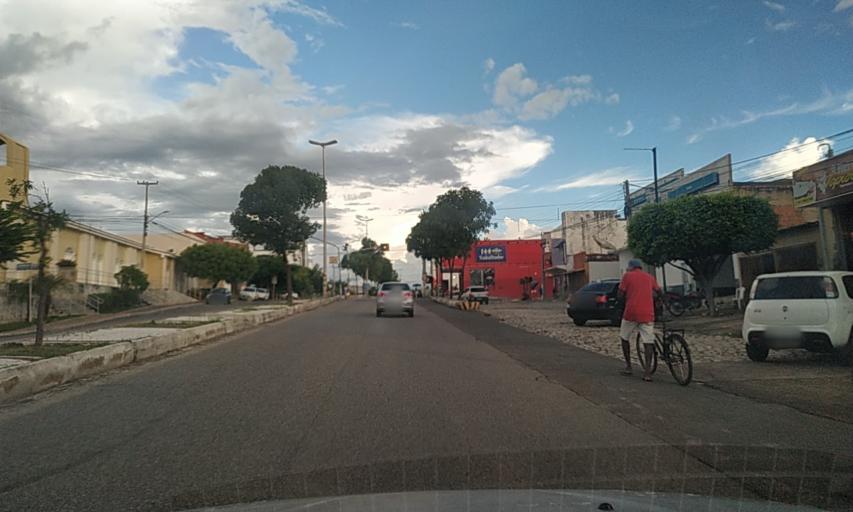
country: BR
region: Rio Grande do Norte
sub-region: Mossoro
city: Mossoro
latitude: -5.2062
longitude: -37.3357
